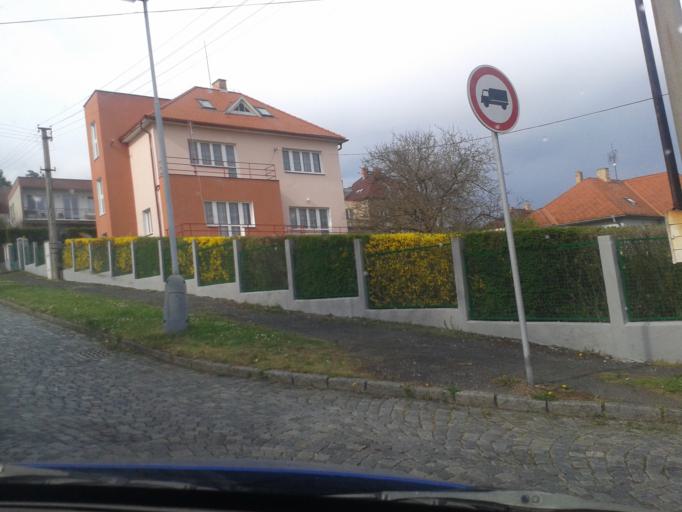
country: CZ
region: Central Bohemia
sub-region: Okres Beroun
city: Beroun
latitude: 49.9699
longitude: 14.0653
